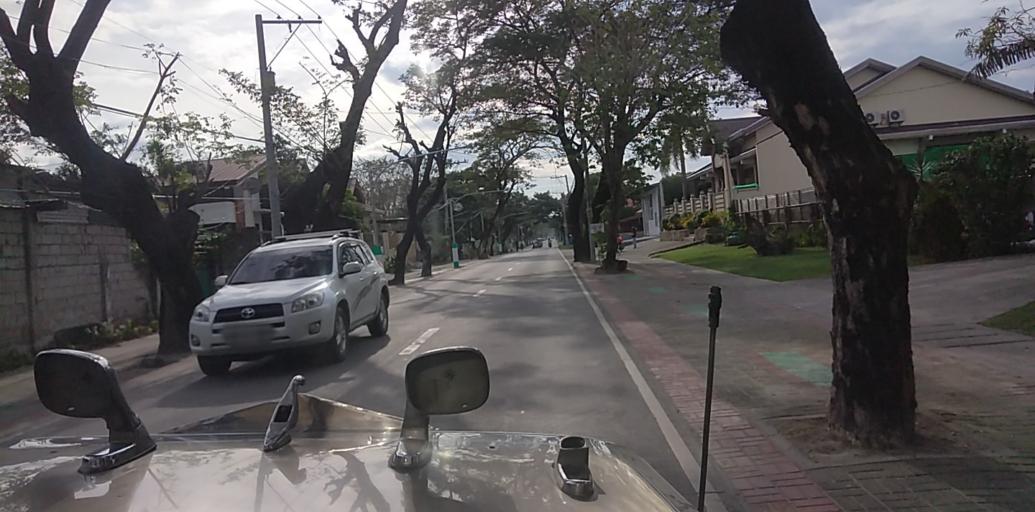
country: PH
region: Central Luzon
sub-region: Province of Pampanga
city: Minalin
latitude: 14.9805
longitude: 120.6945
